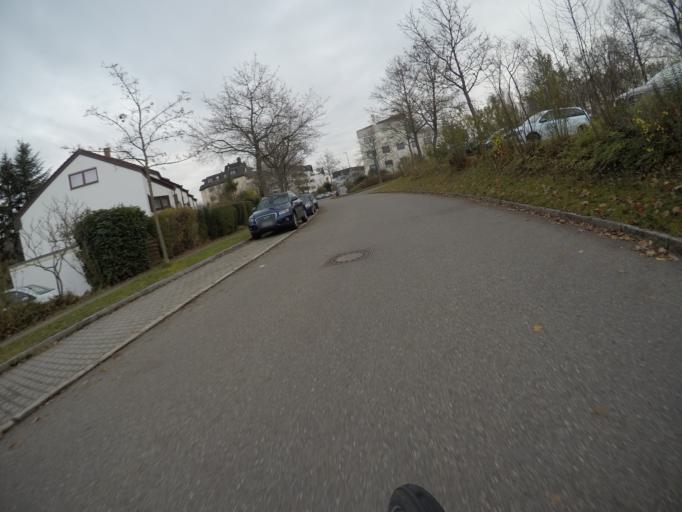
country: DE
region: Baden-Wuerttemberg
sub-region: Regierungsbezirk Stuttgart
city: Leinfelden-Echterdingen
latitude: 48.7013
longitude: 9.1320
